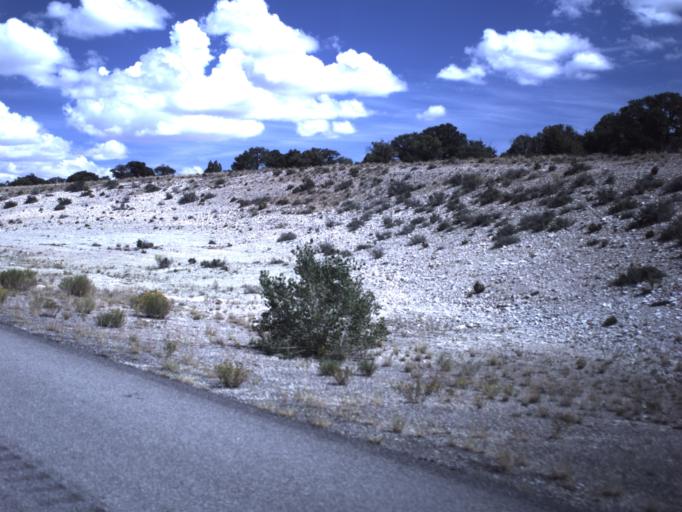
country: US
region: Utah
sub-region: Emery County
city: Ferron
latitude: 38.8462
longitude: -110.9427
